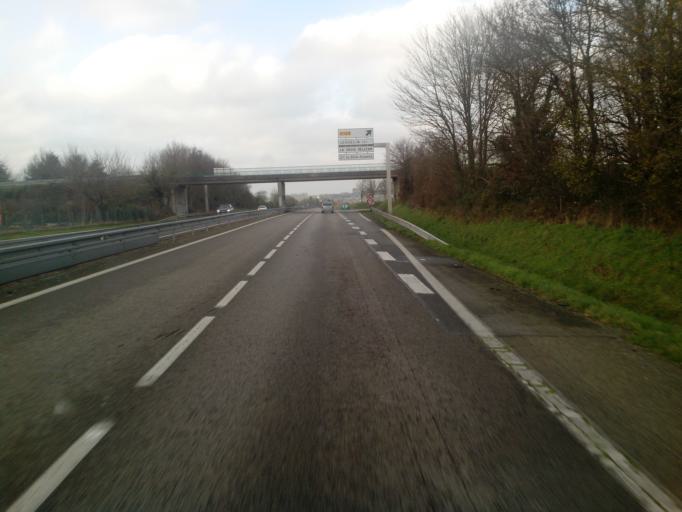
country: FR
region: Brittany
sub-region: Departement du Morbihan
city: Josselin
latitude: 47.9520
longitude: -2.5287
